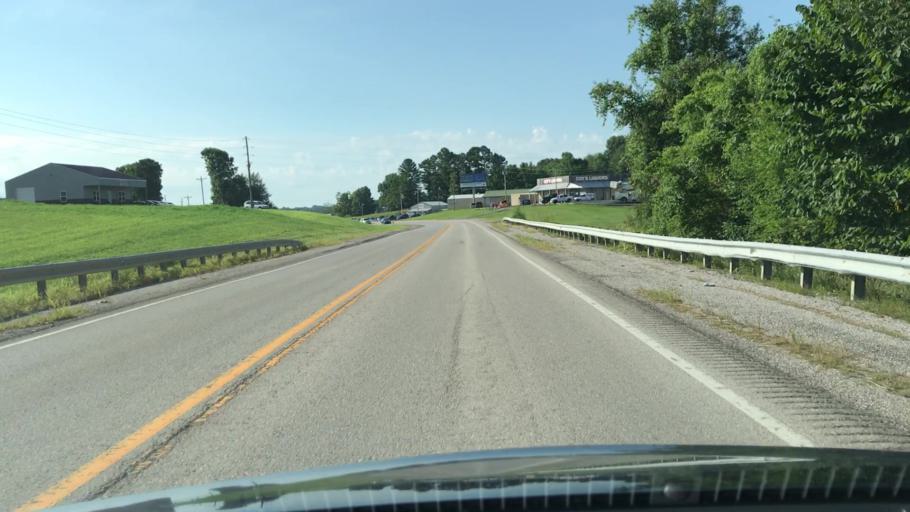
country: US
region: Kentucky
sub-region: Metcalfe County
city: Edmonton
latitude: 36.9915
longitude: -85.6567
